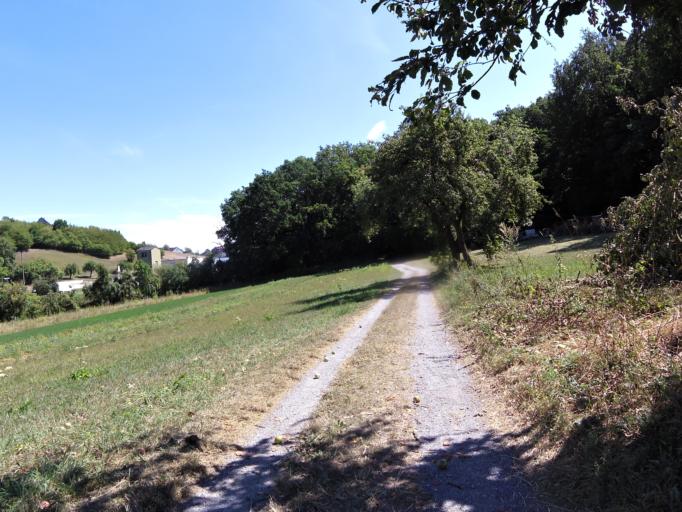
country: DE
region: Bavaria
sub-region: Regierungsbezirk Unterfranken
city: Theilheim
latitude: 49.7528
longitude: 10.0134
